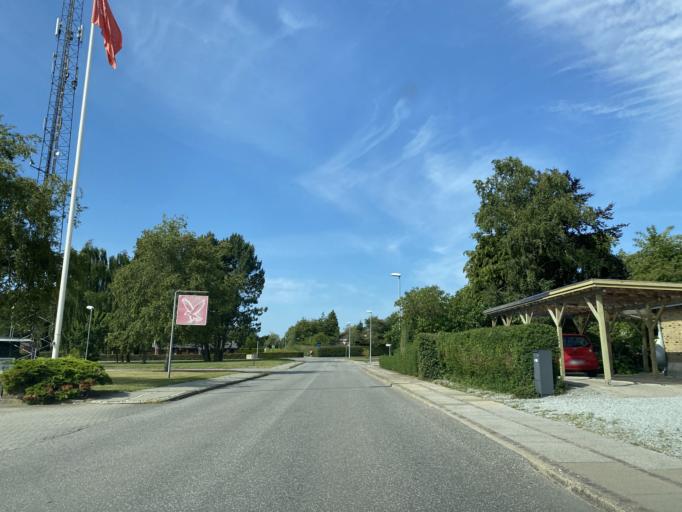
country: DK
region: Central Jutland
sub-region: Favrskov Kommune
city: Hammel
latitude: 56.2580
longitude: 9.8595
